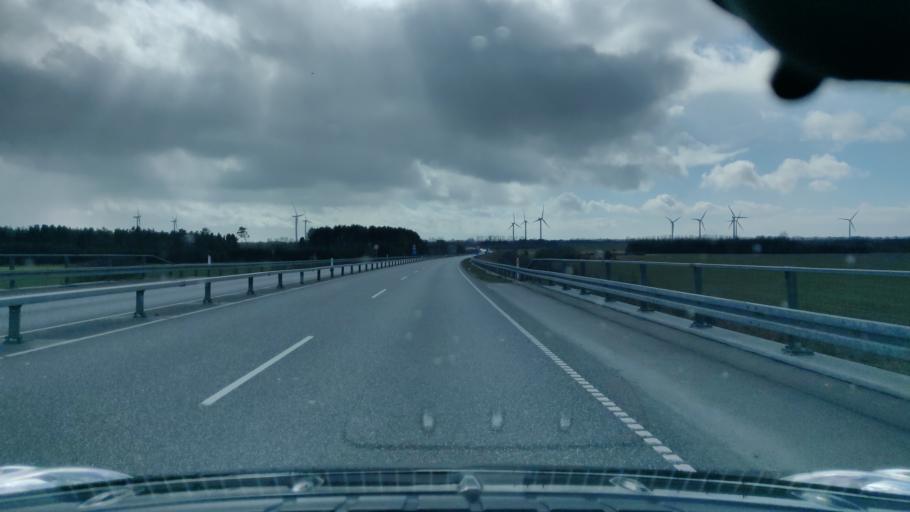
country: DK
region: Zealand
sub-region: Odsherred Kommune
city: Asnaes
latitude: 55.7811
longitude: 11.5837
